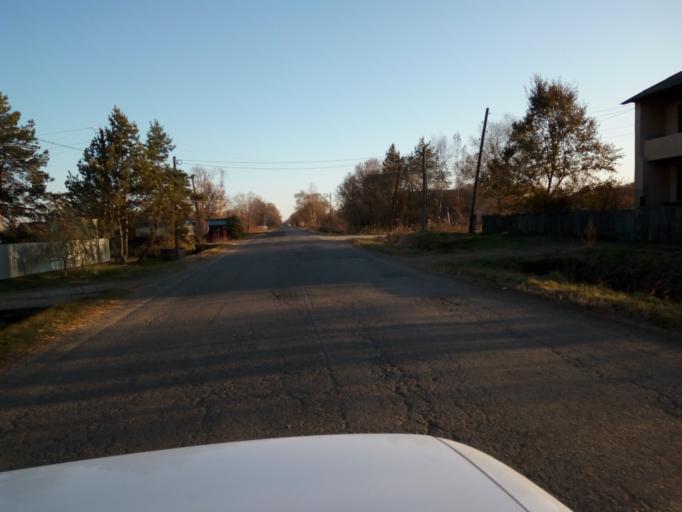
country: RU
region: Primorskiy
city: Lazo
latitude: 45.8674
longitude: 133.6444
